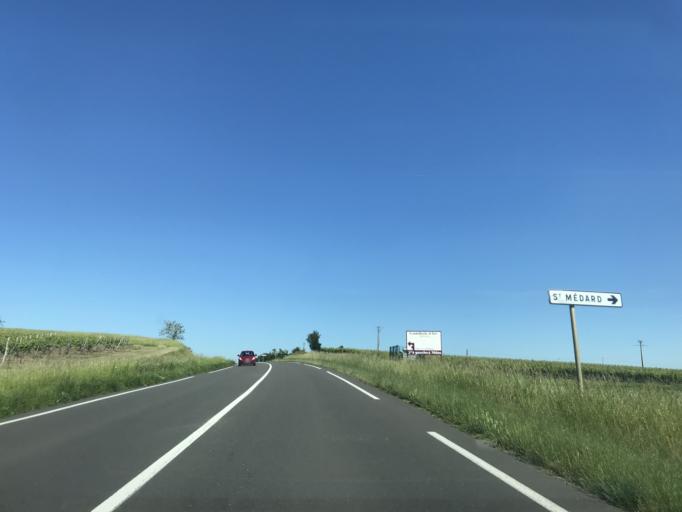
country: FR
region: Poitou-Charentes
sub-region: Departement de la Charente
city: Barbezieux-Saint-Hilaire
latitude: 45.4915
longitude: -0.1954
